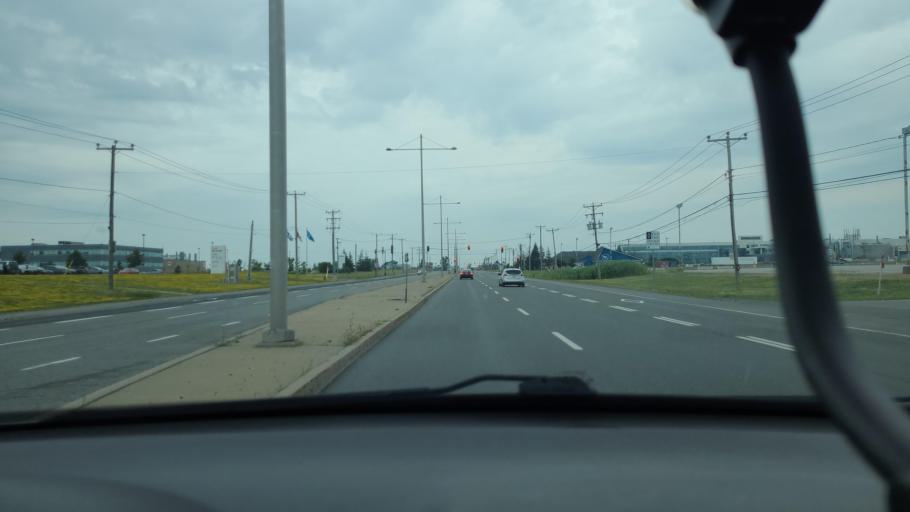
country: CA
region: Quebec
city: Dorval
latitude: 45.4771
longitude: -73.7295
